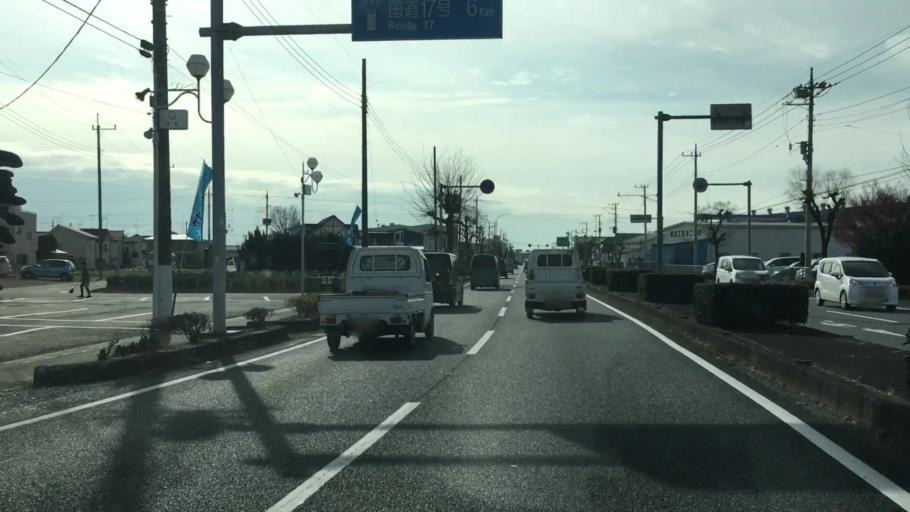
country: JP
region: Saitama
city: Menuma
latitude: 36.2271
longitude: 139.3703
